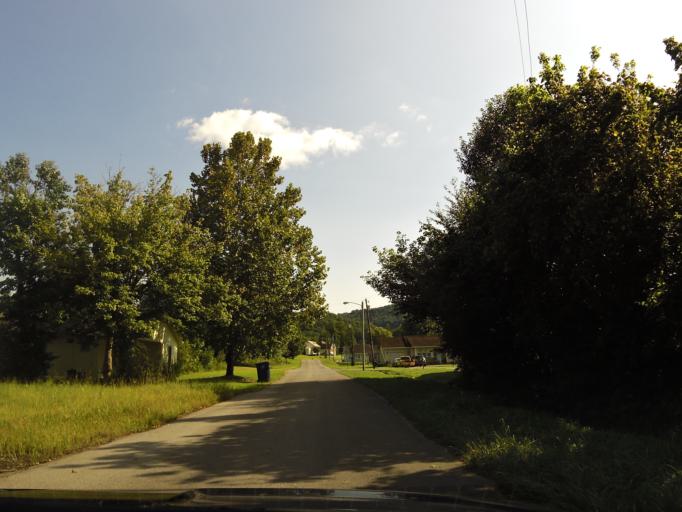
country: US
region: Kentucky
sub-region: Bell County
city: Middlesboro
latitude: 36.6015
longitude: -83.7261
